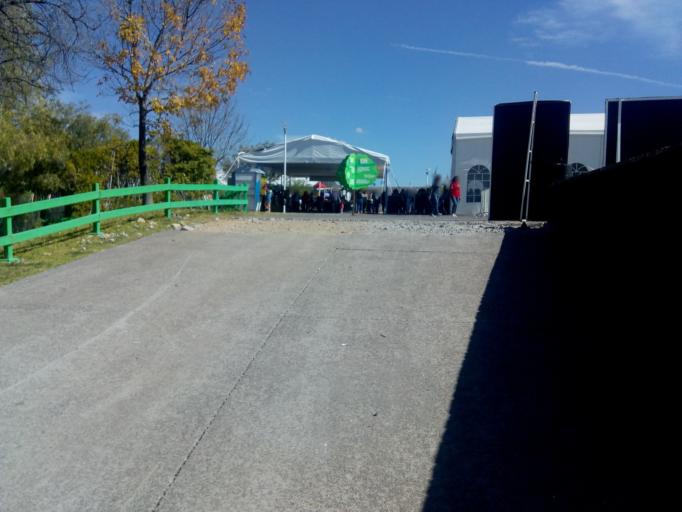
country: MX
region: Guanajuato
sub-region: Silao de la Victoria
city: Aguas Buenas
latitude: 20.9542
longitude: -101.3633
